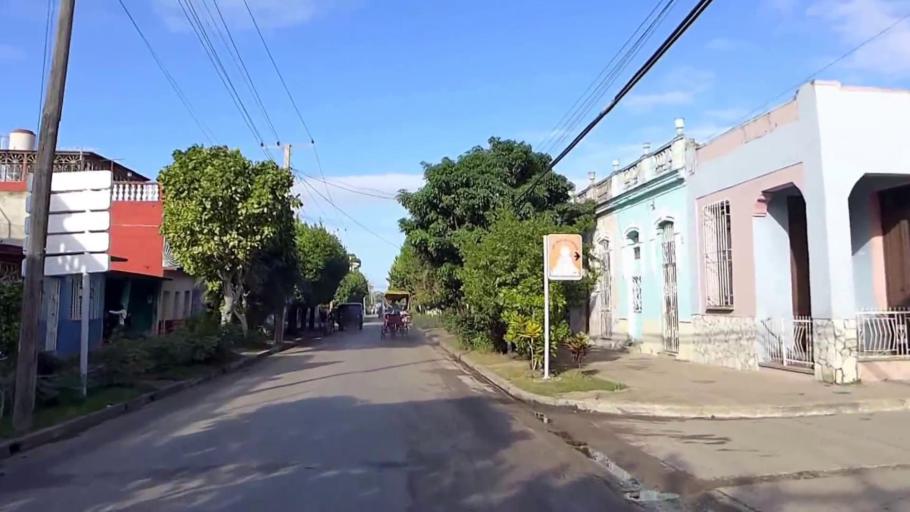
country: CU
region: Camaguey
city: Camaguey
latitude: 21.3852
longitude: -77.9279
